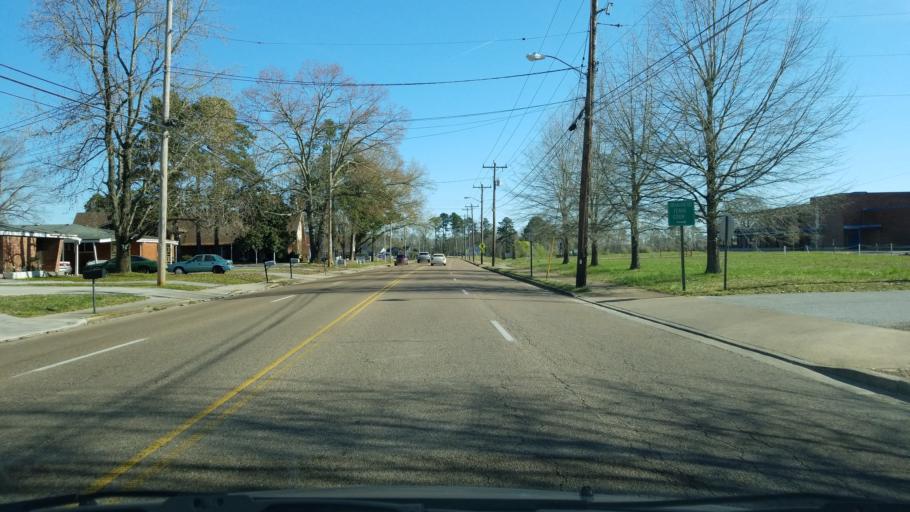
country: US
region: Tennessee
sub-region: Hamilton County
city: East Ridge
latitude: 35.0270
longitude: -85.2205
